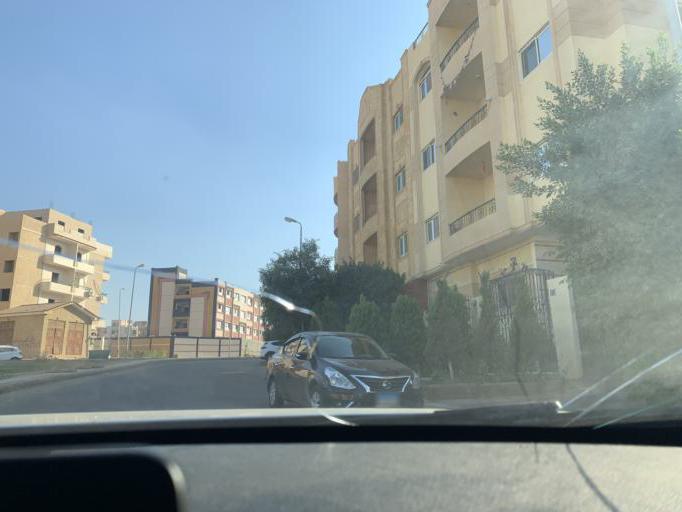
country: EG
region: Muhafazat al Qalyubiyah
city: Al Khankah
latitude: 30.0038
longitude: 31.4827
